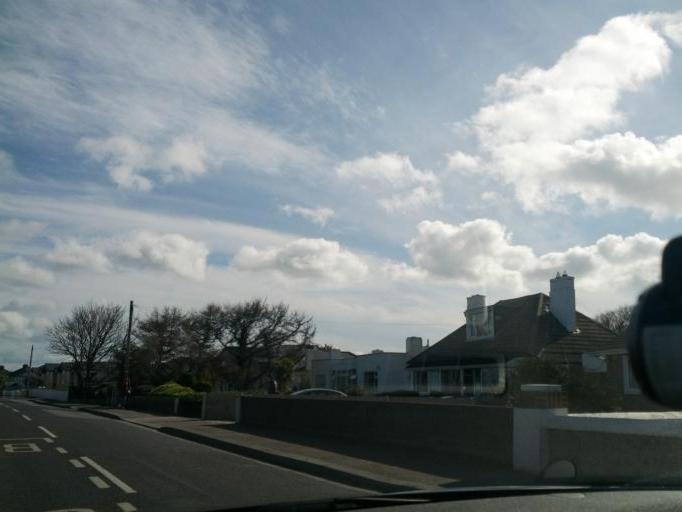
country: IE
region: Leinster
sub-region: Fingal County
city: Baldoyle
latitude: 53.3960
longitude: -6.1247
